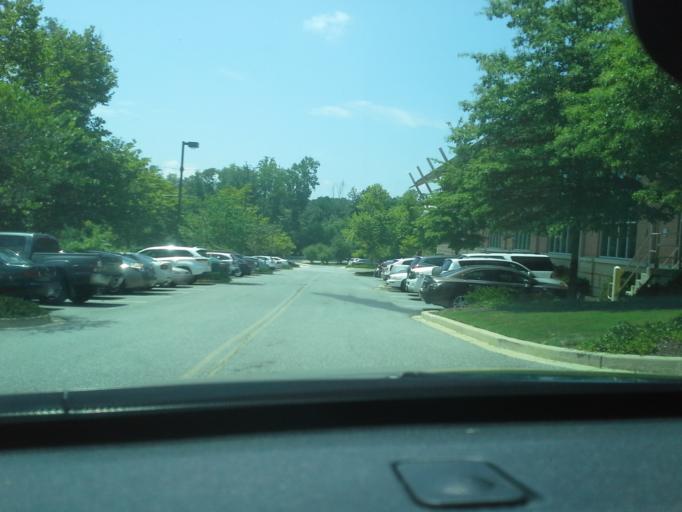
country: US
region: Maryland
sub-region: Calvert County
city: Prince Frederick
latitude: 38.5560
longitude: -76.5988
